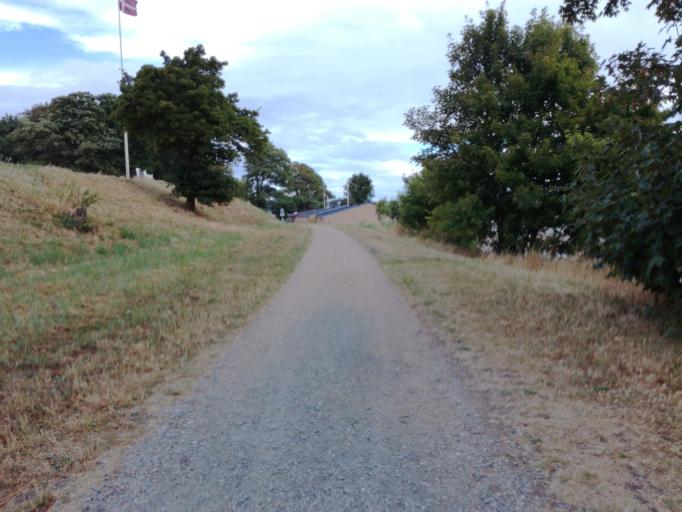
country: DK
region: South Denmark
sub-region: Fredericia Kommune
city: Fredericia
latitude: 55.5594
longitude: 9.7681
